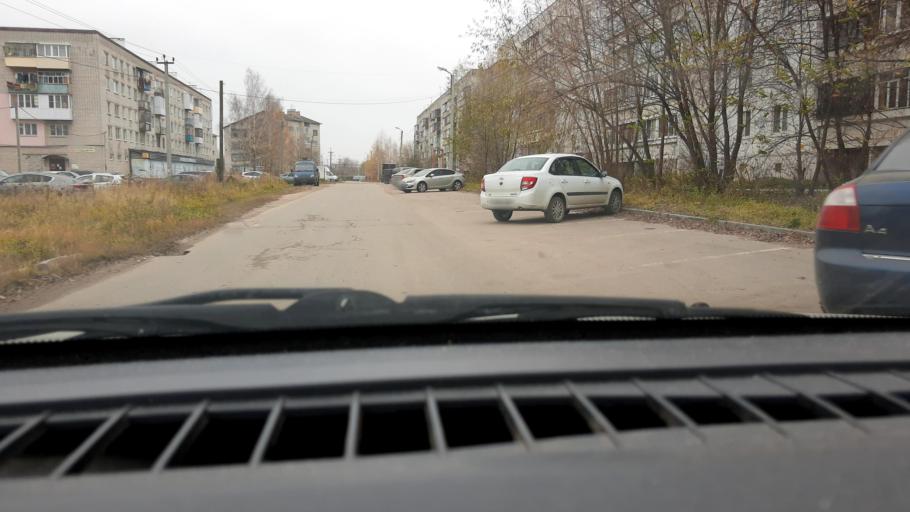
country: RU
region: Nizjnij Novgorod
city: Afonino
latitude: 56.2095
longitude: 44.0981
